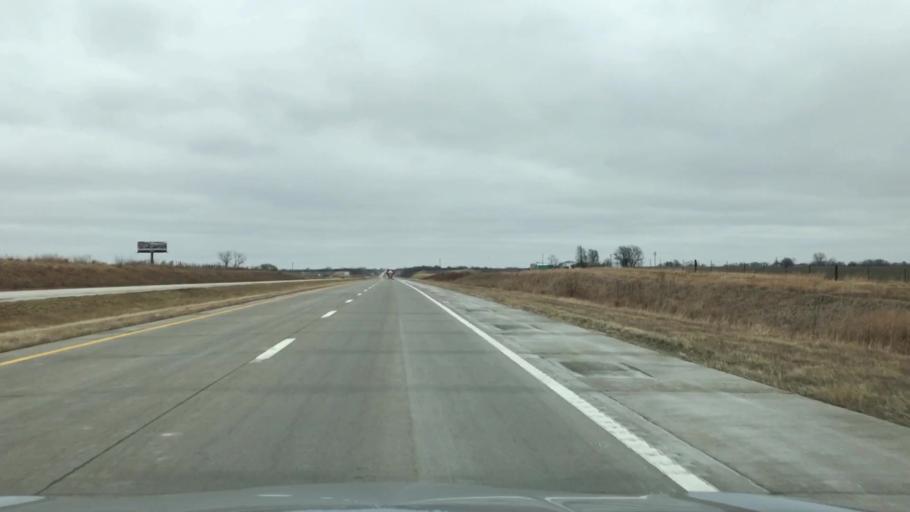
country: US
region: Missouri
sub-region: Caldwell County
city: Hamilton
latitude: 39.7335
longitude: -93.9903
